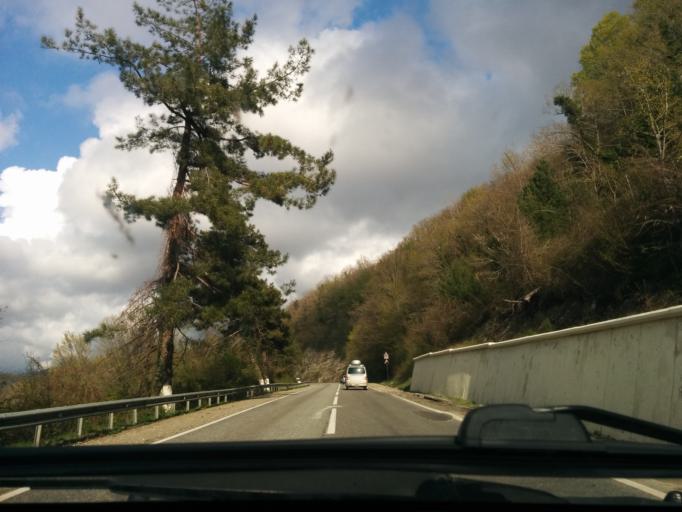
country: RU
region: Krasnodarskiy
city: Novomikhaylovskiy
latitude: 44.2559
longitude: 38.8712
